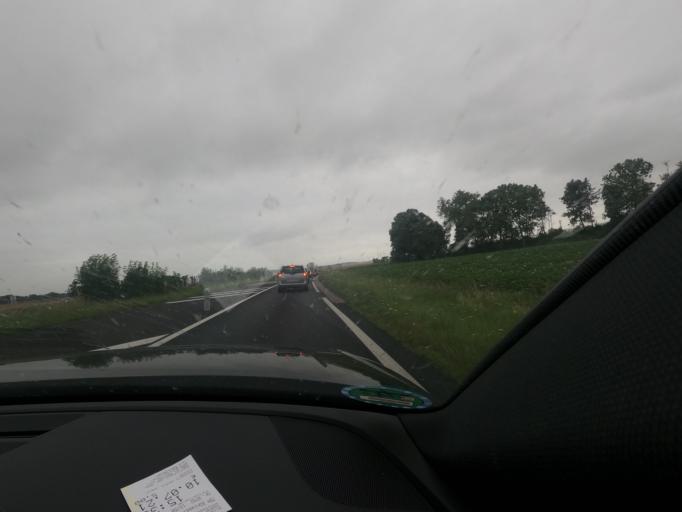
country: FR
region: Picardie
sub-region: Departement de la Somme
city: Moreuil
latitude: 49.8294
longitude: 2.4604
